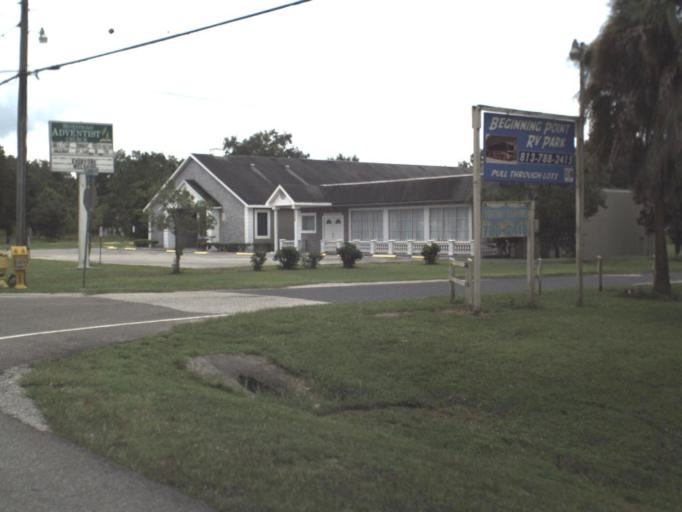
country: US
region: Florida
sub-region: Pasco County
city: Zephyrhills West
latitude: 28.2194
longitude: -82.2639
